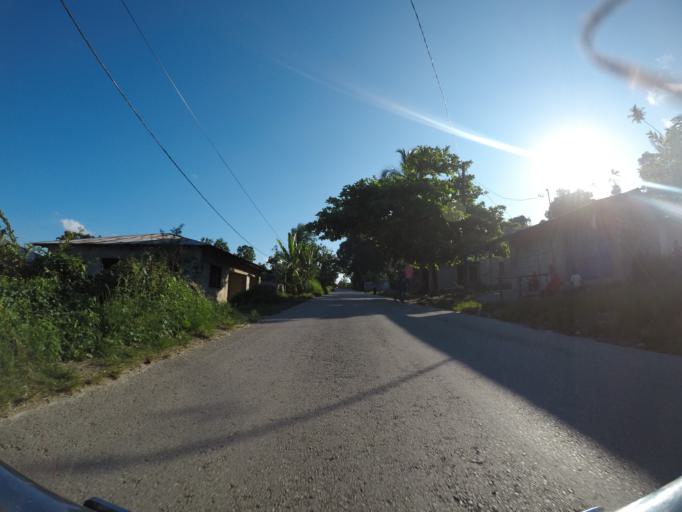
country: TZ
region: Pemba South
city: Mtambile
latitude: -5.3196
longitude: 39.7426
